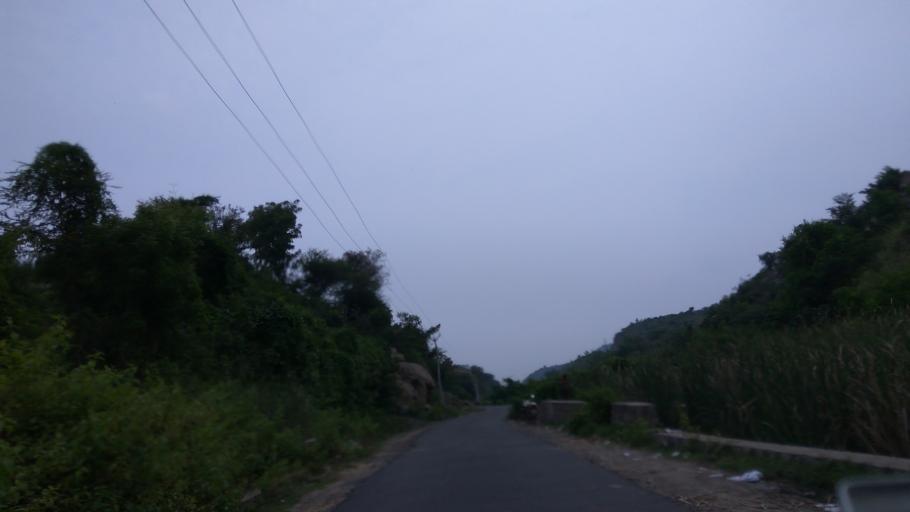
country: IN
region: Tamil Nadu
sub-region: Dharmapuri
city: Dharmapuri
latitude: 12.0194
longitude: 78.1213
